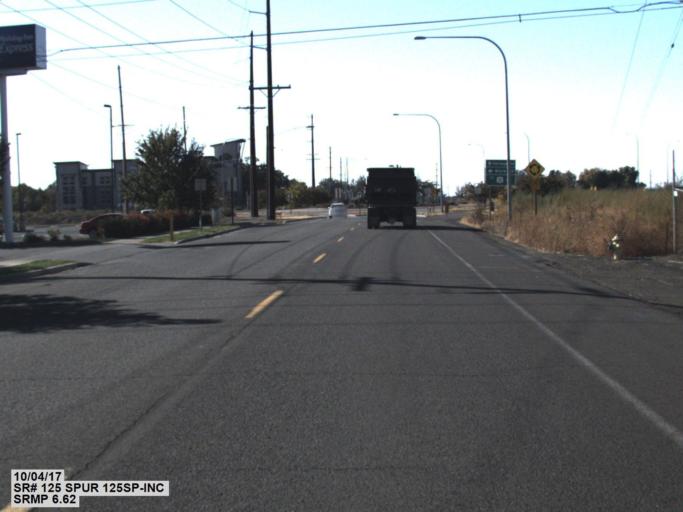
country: US
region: Washington
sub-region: Walla Walla County
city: College Place
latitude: 46.0081
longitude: -118.3901
